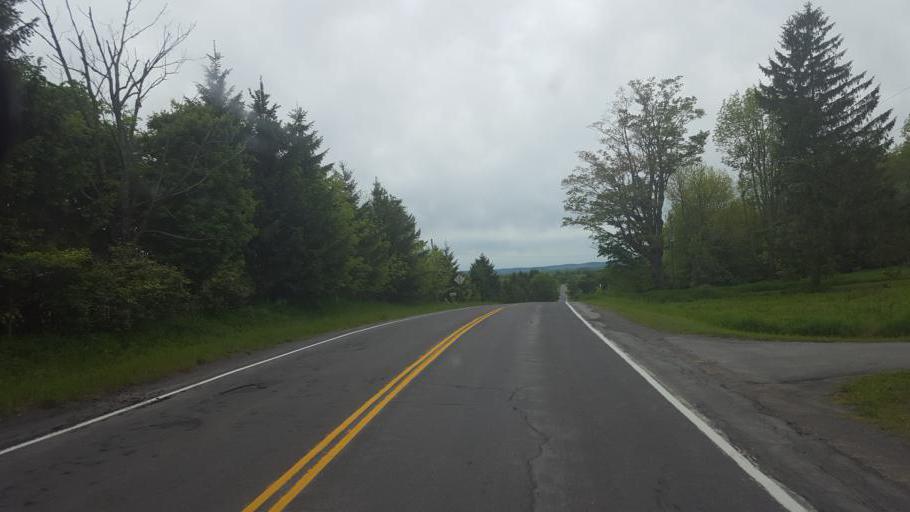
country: US
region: New York
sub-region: Herkimer County
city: Ilion
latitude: 42.9320
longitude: -75.0579
